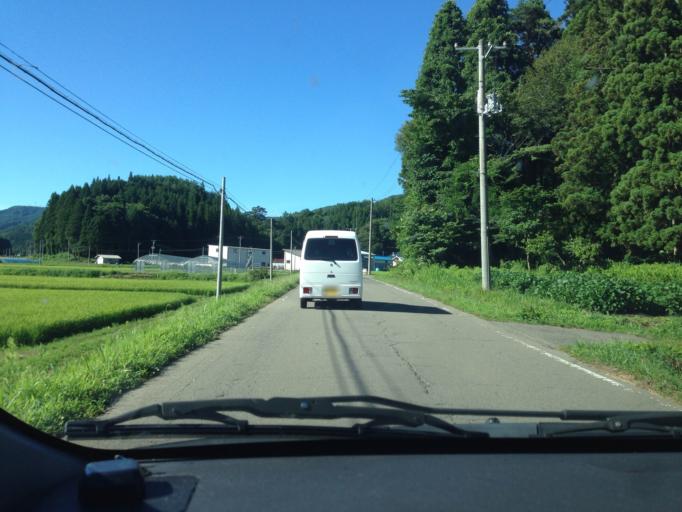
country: JP
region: Fukushima
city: Inawashiro
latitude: 37.3937
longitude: 140.0670
